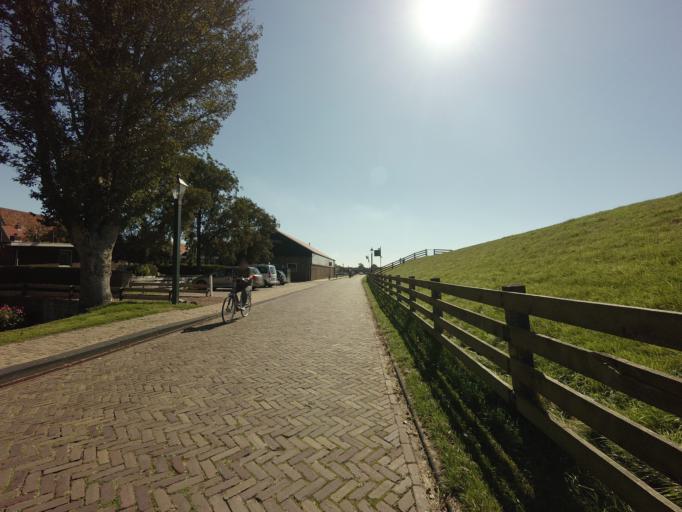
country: NL
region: Friesland
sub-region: Sudwest Fryslan
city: Koudum
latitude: 52.9415
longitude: 5.4000
